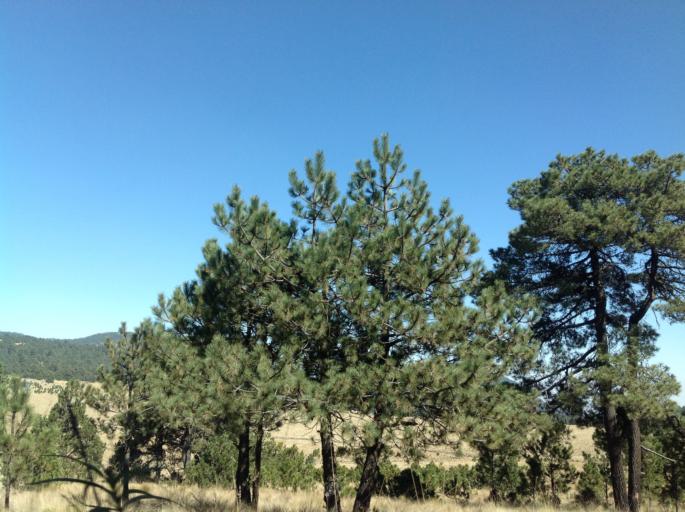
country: MX
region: Mexico
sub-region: Amecameca
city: San Diego Huehuecalco
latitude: 19.0903
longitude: -98.6473
